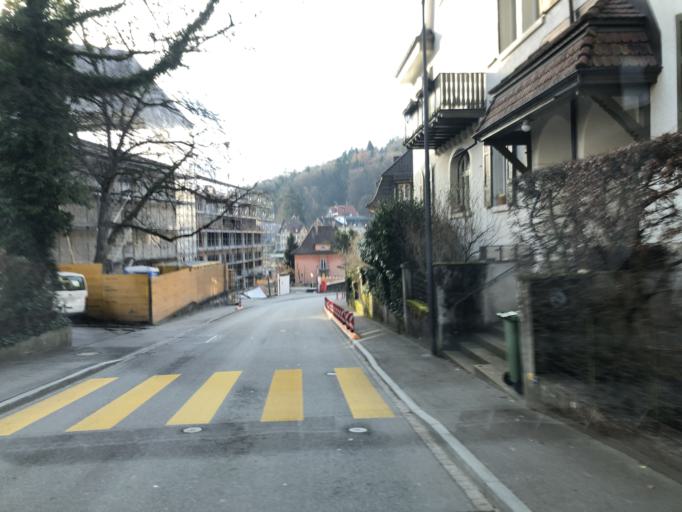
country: CH
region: Aargau
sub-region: Bezirk Baden
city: Baden
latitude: 47.4715
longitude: 8.3013
